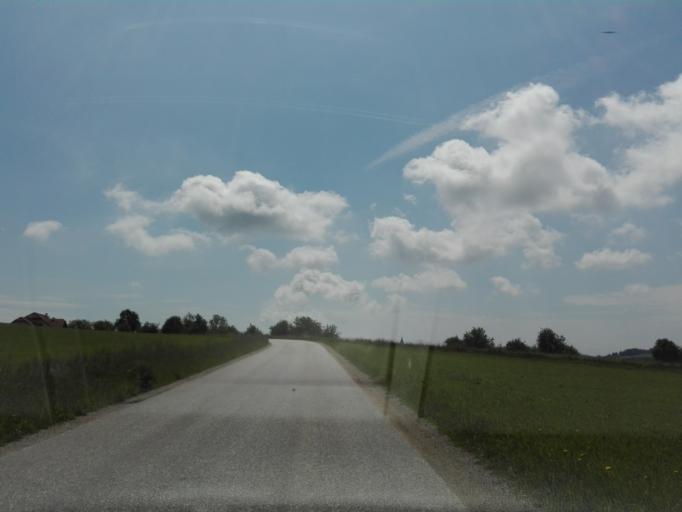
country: AT
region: Upper Austria
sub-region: Politischer Bezirk Rohrbach
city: Atzesberg
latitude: 48.4179
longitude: 13.9127
